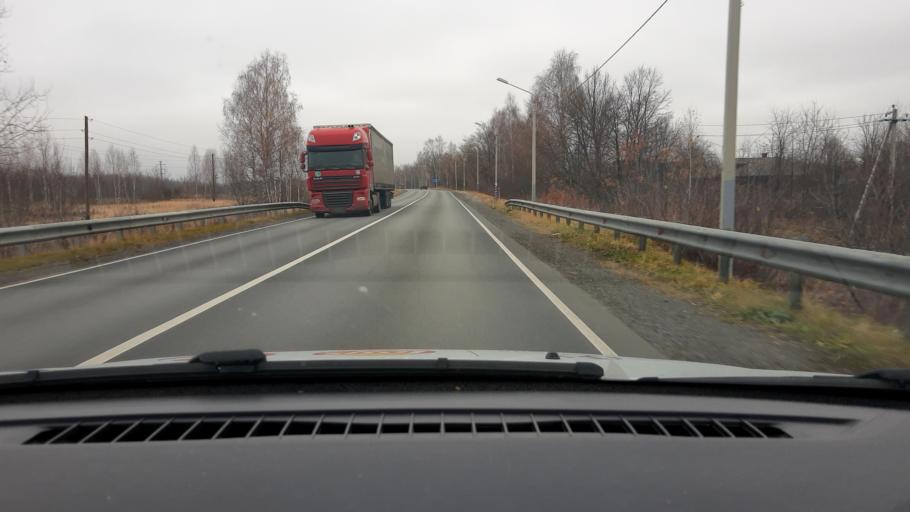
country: RU
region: Nizjnij Novgorod
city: Gorodets
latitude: 56.5945
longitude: 43.4604
